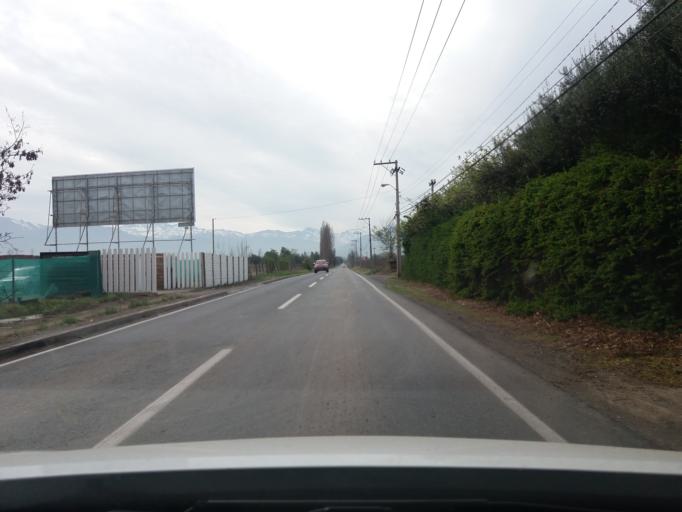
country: CL
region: Valparaiso
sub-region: Provincia de Los Andes
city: Los Andes
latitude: -32.8211
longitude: -70.6744
